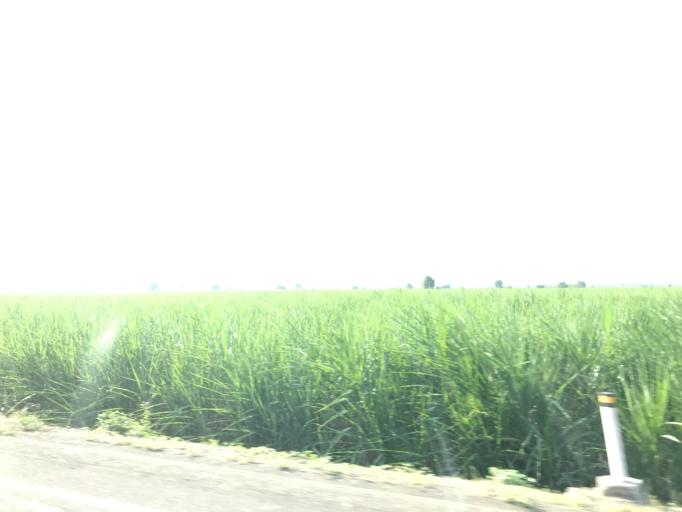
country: PE
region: Lambayeque
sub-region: Provincia de Chiclayo
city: Chongoyape
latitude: -6.6774
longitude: -79.4454
